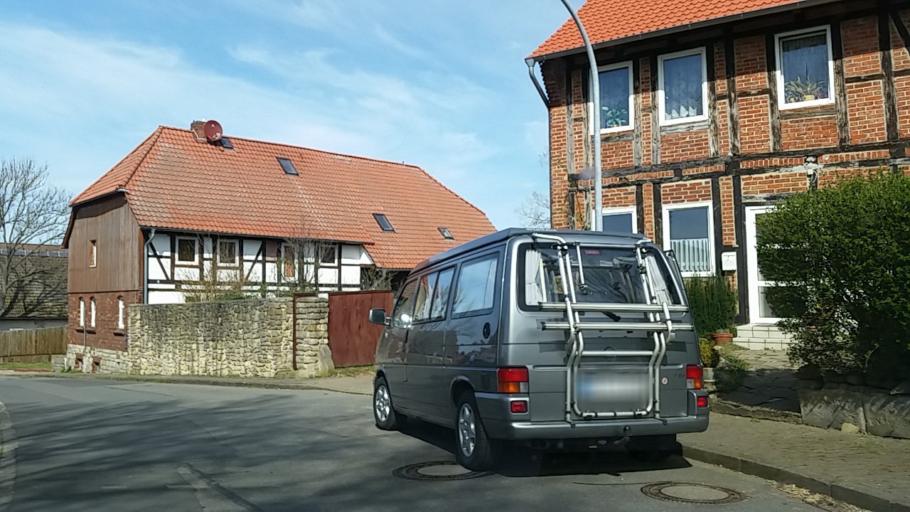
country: DE
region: Lower Saxony
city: Querenhorst
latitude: 52.3578
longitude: 10.9685
